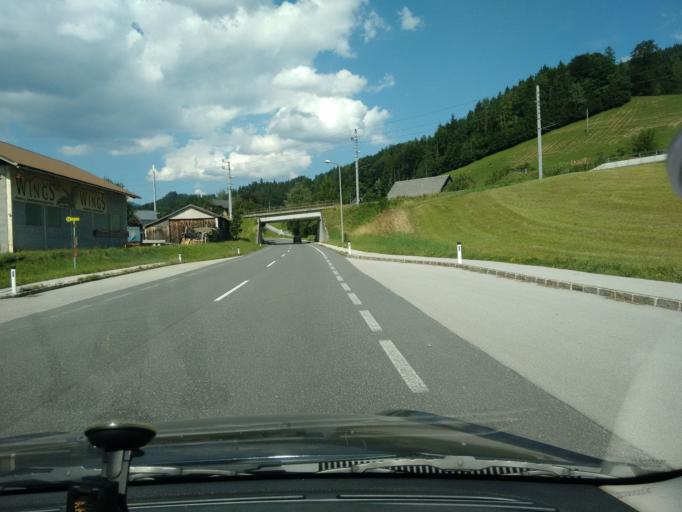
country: AT
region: Upper Austria
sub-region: Politischer Bezirk Kirchdorf an der Krems
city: Rossleithen
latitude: 47.6702
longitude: 14.3475
